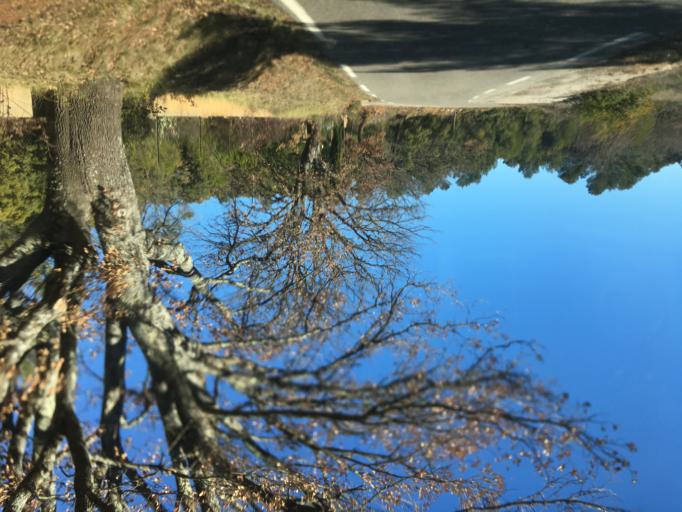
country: FR
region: Provence-Alpes-Cote d'Azur
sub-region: Departement du Var
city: Barjols
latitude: 43.5940
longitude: 6.0615
